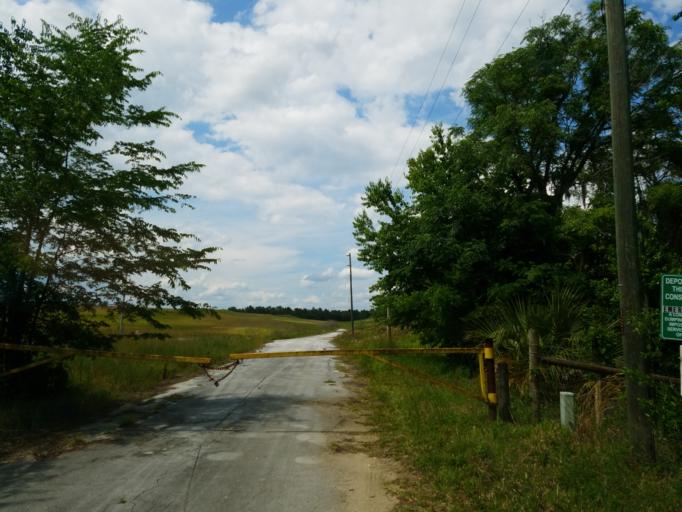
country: US
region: Florida
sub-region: Hernando County
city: Hill 'n Dale
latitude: 28.5377
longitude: -82.2656
